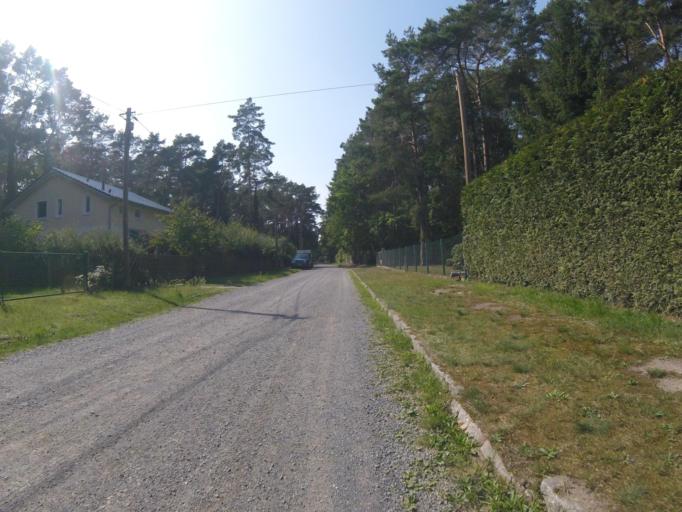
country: DE
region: Brandenburg
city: Bestensee
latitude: 52.2618
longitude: 13.7450
